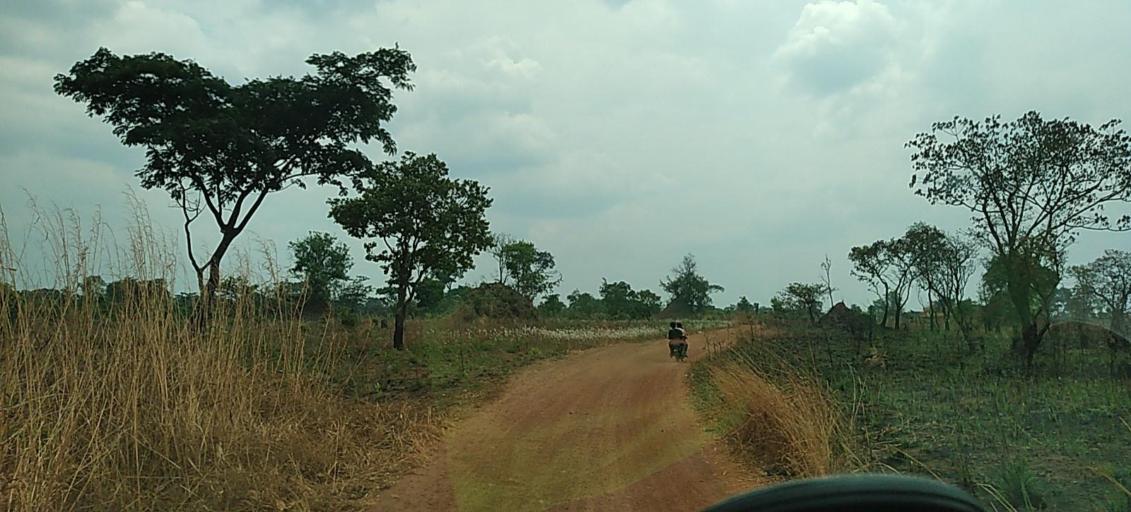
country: ZM
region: North-Western
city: Kansanshi
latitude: -12.0858
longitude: 26.3637
